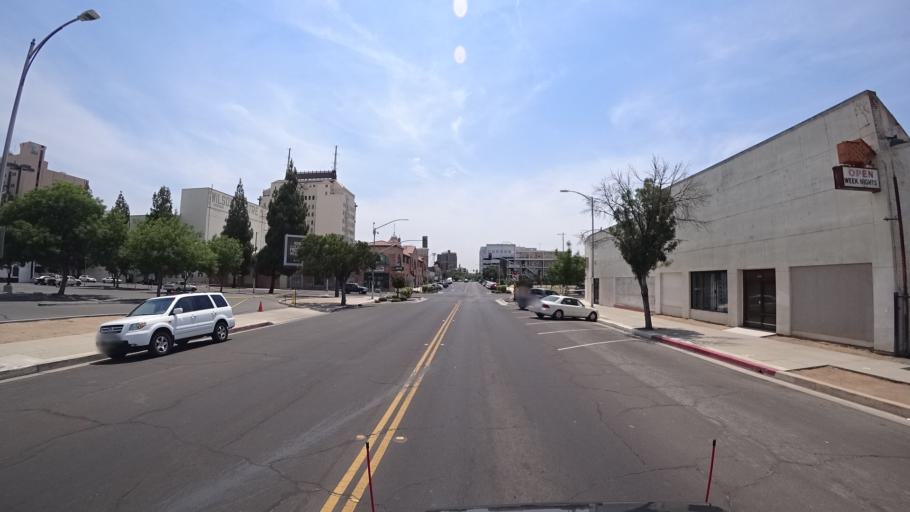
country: US
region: California
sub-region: Fresno County
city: Fresno
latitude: 36.7385
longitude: -119.7970
